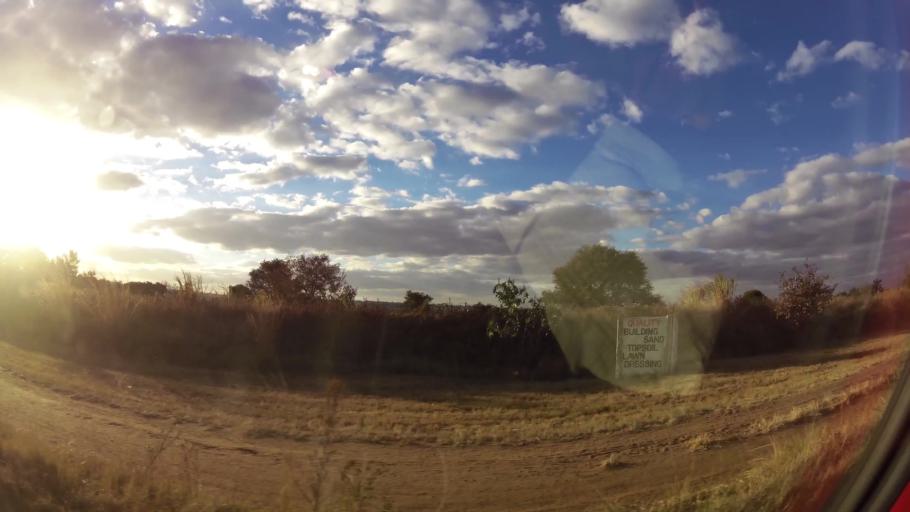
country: ZA
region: Gauteng
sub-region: City of Johannesburg Metropolitan Municipality
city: Midrand
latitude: -25.9558
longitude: 28.1791
